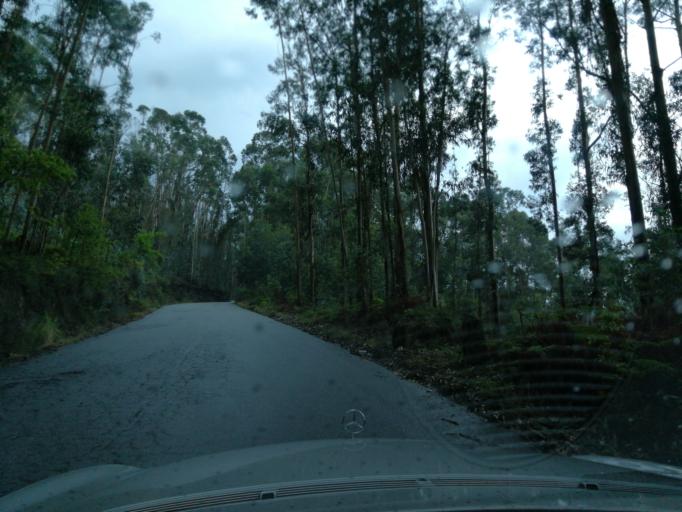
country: PT
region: Braga
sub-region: Braga
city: Oliveira
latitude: 41.4689
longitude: -8.4391
